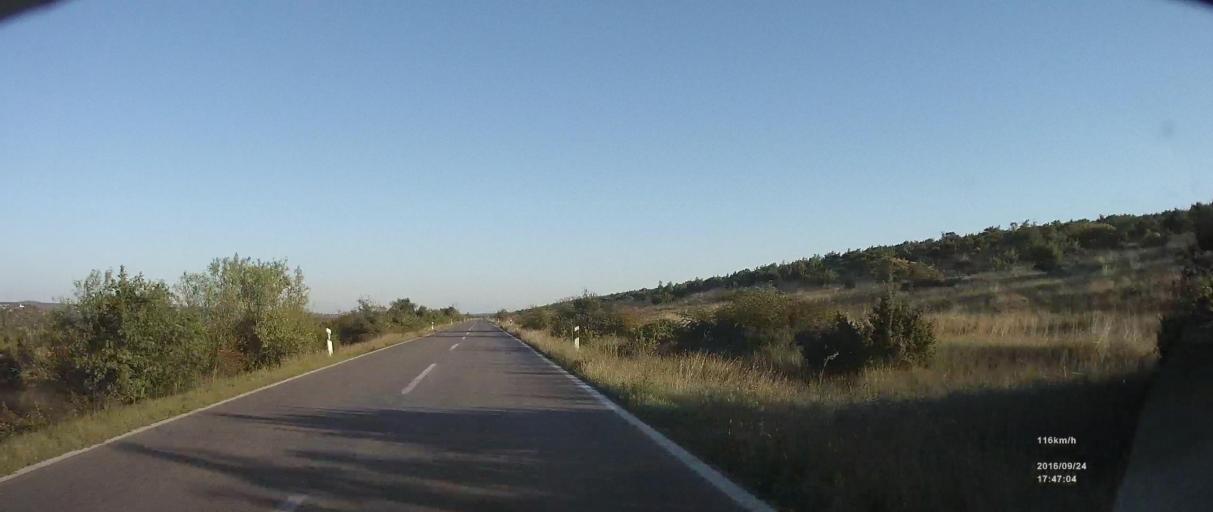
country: HR
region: Zadarska
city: Polaca
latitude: 44.0798
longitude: 15.5172
